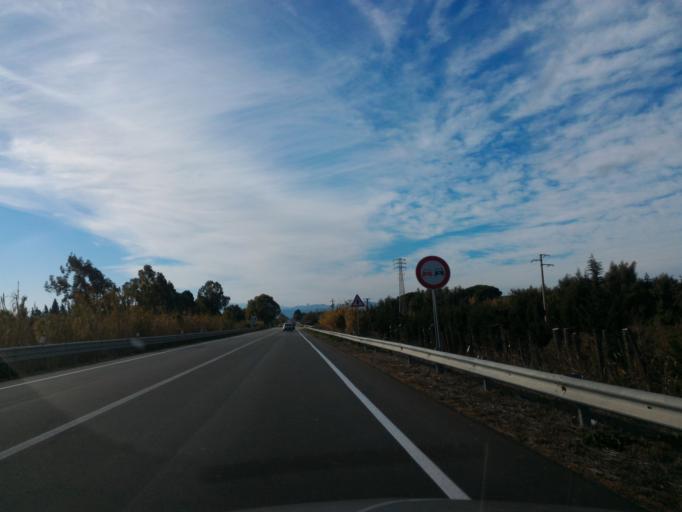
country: IT
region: Calabria
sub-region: Provincia di Catanzaro
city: Barone
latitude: 38.8625
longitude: 16.6798
